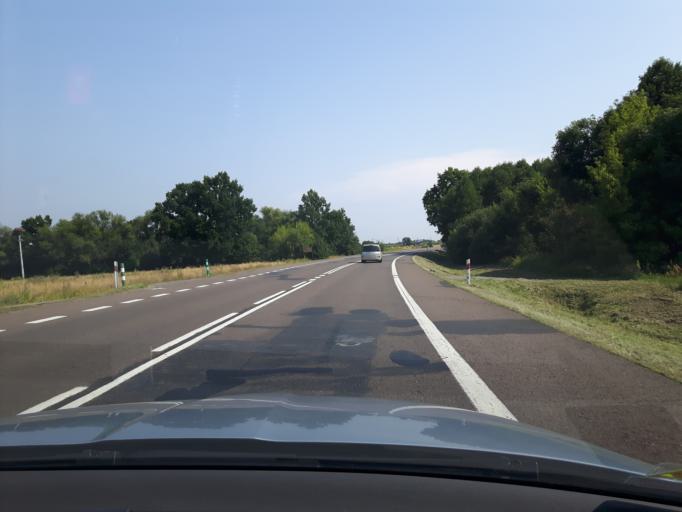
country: PL
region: Masovian Voivodeship
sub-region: Powiat ciechanowski
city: Glinojeck
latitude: 52.7877
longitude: 20.2811
